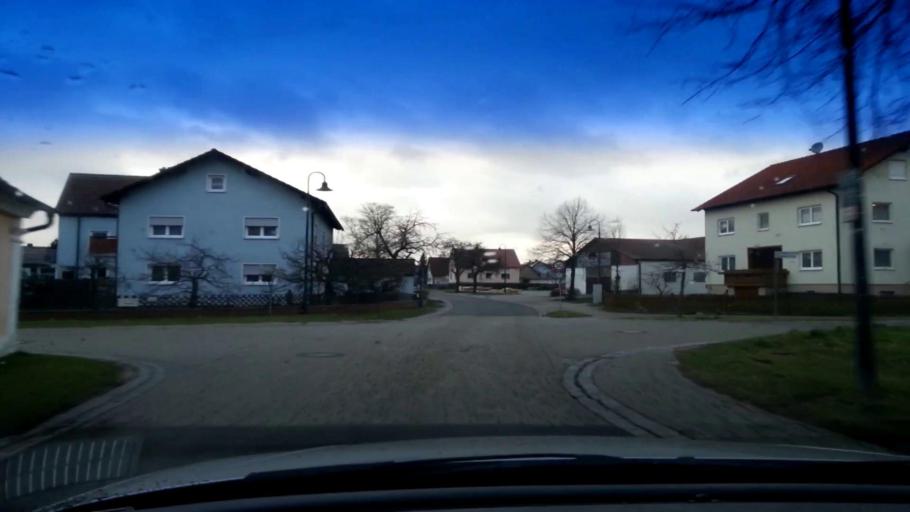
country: DE
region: Bavaria
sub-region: Upper Franconia
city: Frensdorf
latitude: 49.8240
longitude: 10.8384
